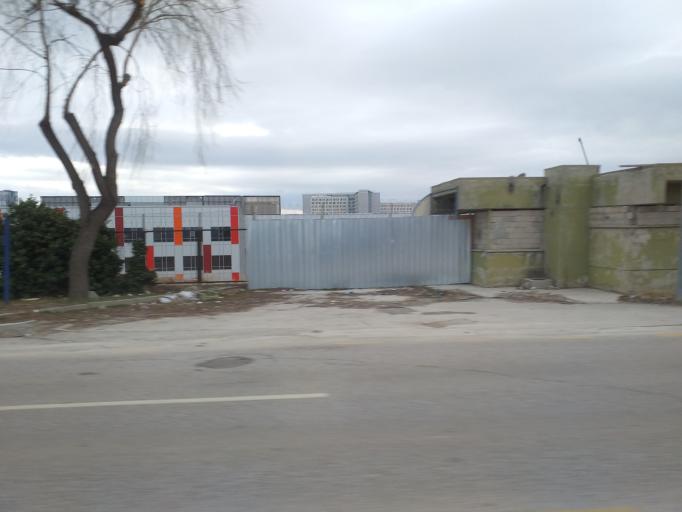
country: TR
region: Ankara
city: Ankara
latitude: 39.9634
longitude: 32.8212
